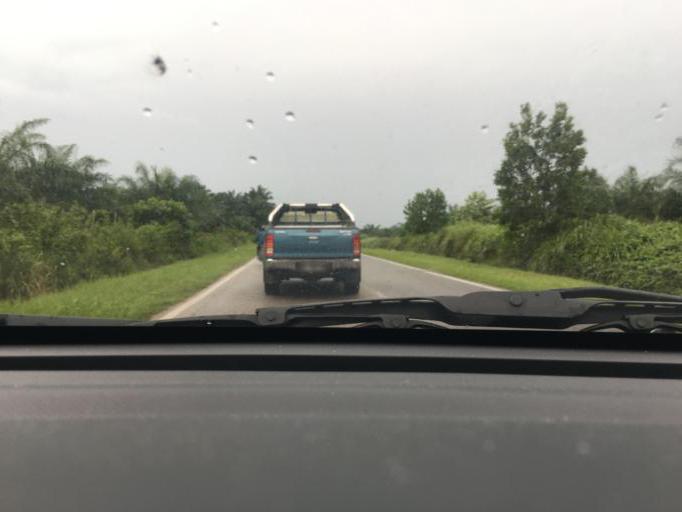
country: MY
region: Kedah
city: Bedong
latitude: 5.6596
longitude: 100.6309
